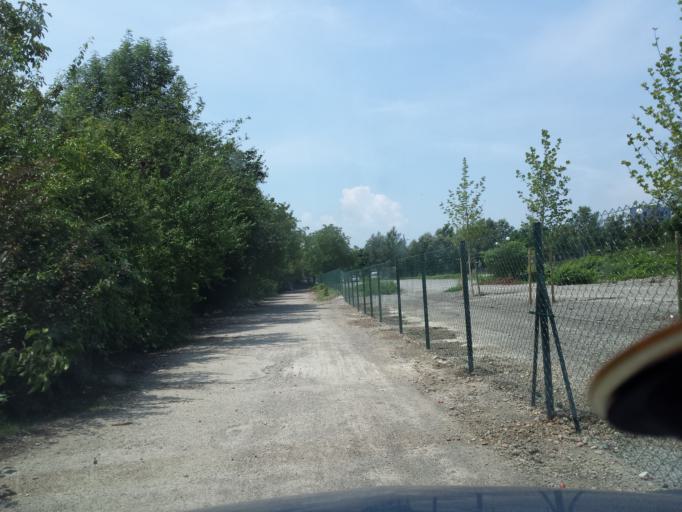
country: HR
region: Grad Zagreb
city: Novi Zagreb
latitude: 45.7916
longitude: 15.9734
